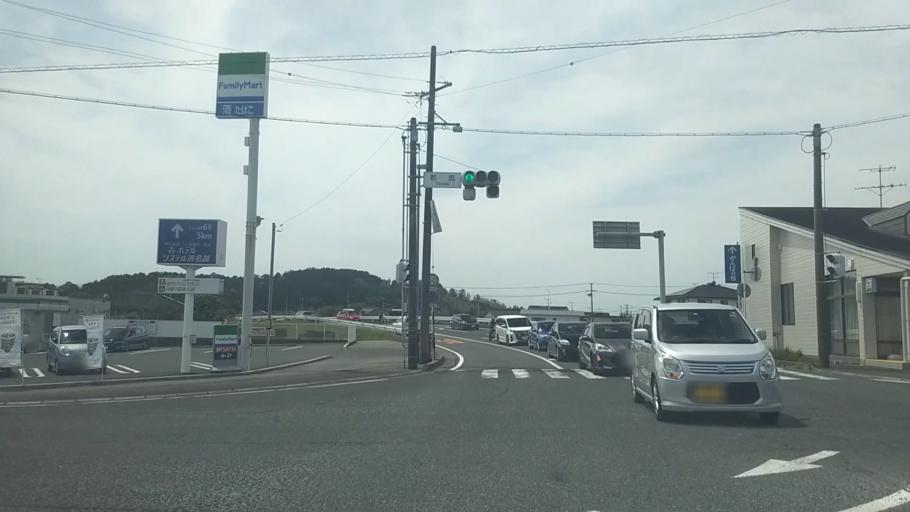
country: JP
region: Shizuoka
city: Kosai-shi
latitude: 34.7921
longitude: 137.5828
